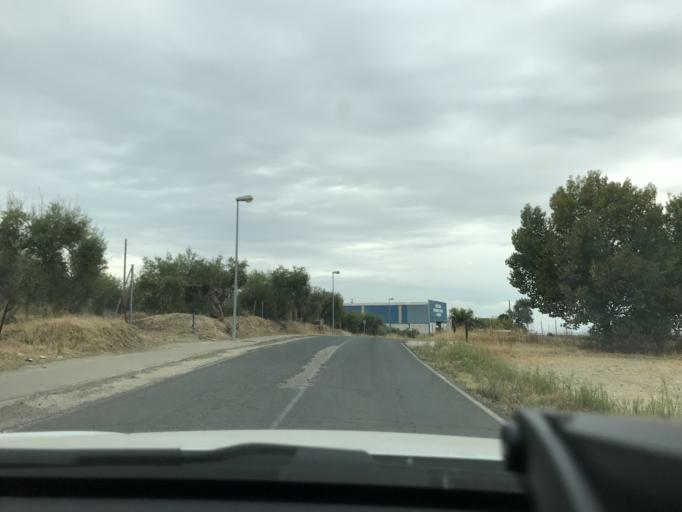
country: ES
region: Andalusia
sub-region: Provincia de Sevilla
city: Villanueva del Rio y Minas
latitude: 37.6467
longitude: -5.7090
